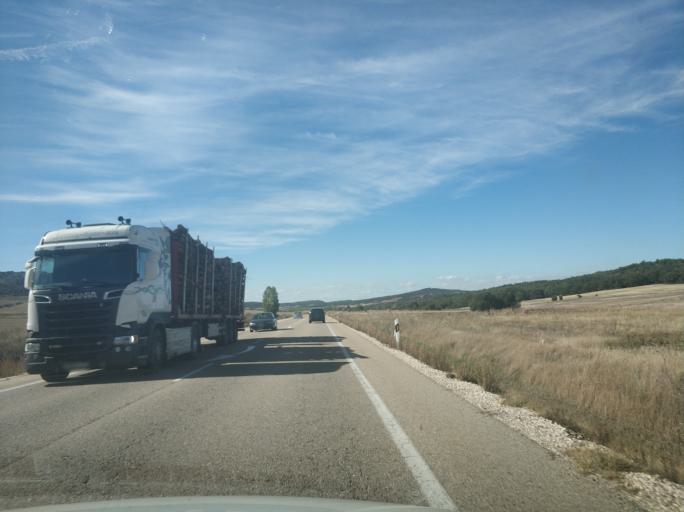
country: ES
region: Castille and Leon
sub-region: Provincia de Burgos
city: Cuevas de San Clemente
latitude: 42.1164
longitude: -3.5316
